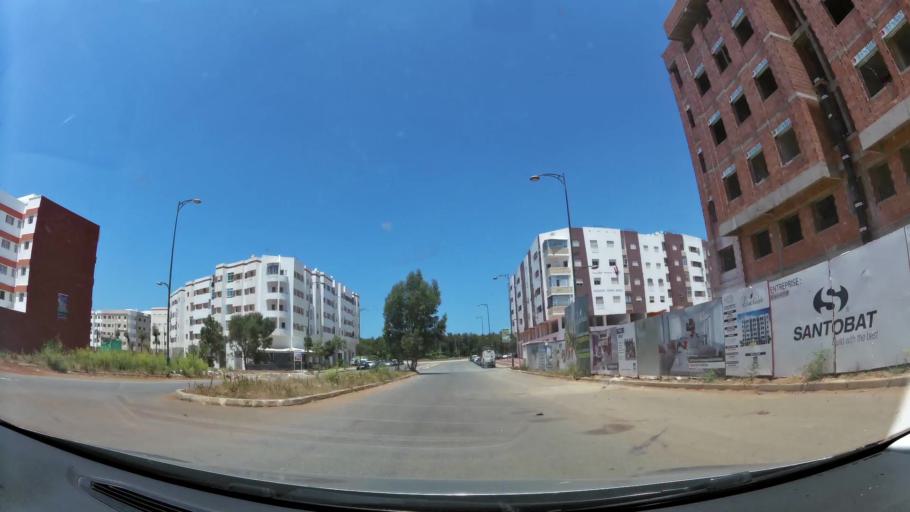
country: MA
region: Gharb-Chrarda-Beni Hssen
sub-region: Kenitra Province
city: Kenitra
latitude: 34.2703
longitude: -6.6278
